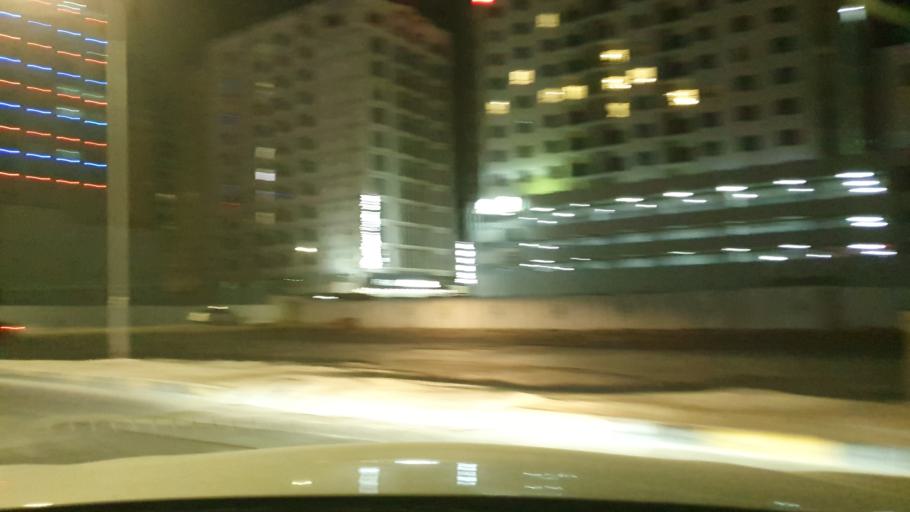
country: BH
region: Manama
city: Manama
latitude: 26.2184
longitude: 50.6059
